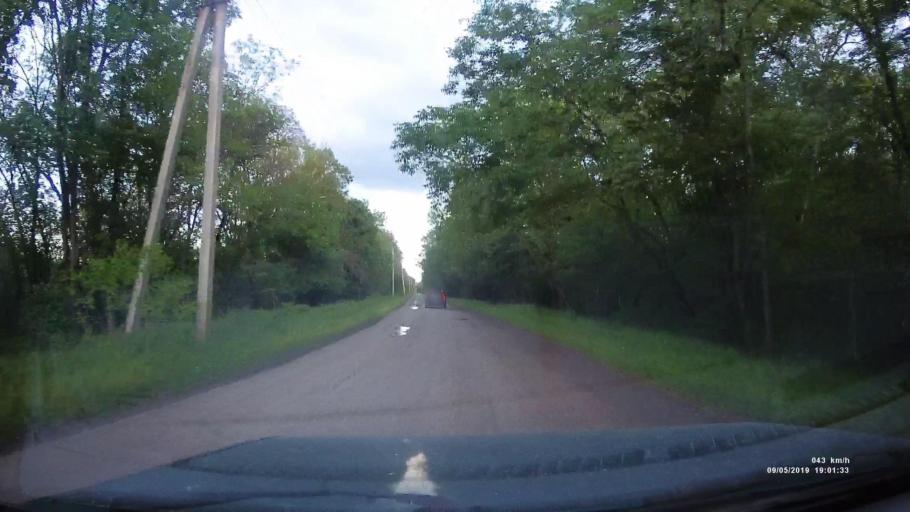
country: RU
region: Krasnodarskiy
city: Kanelovskaya
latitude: 46.7477
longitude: 39.1447
